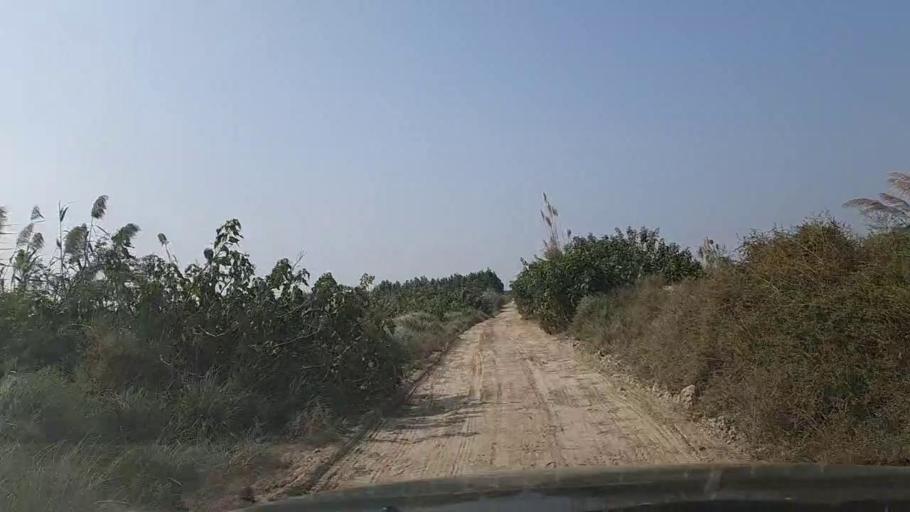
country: PK
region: Sindh
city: Gharo
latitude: 24.7251
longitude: 67.6864
